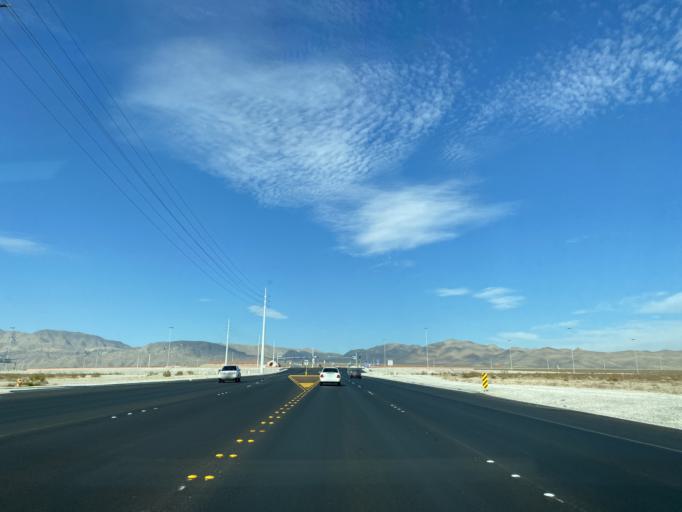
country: US
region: Nevada
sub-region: Clark County
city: Nellis Air Force Base
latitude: 36.2859
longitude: -115.0798
